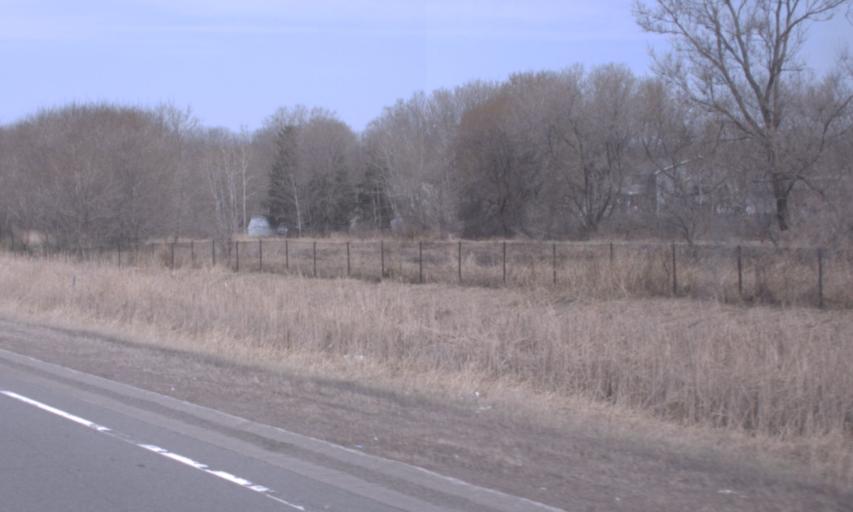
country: US
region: Minnesota
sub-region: Anoka County
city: Coon Rapids
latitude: 45.1567
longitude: -93.2788
